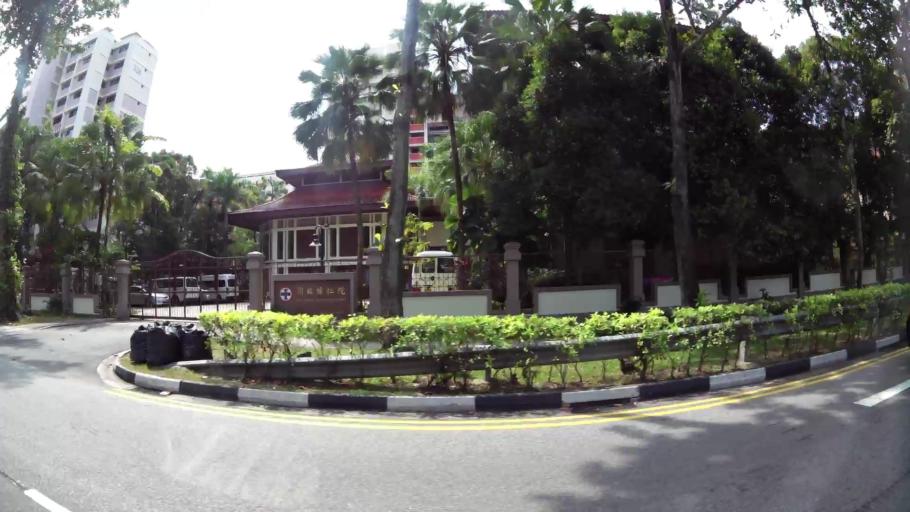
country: MY
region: Johor
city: Johor Bahru
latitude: 1.3499
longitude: 103.7291
